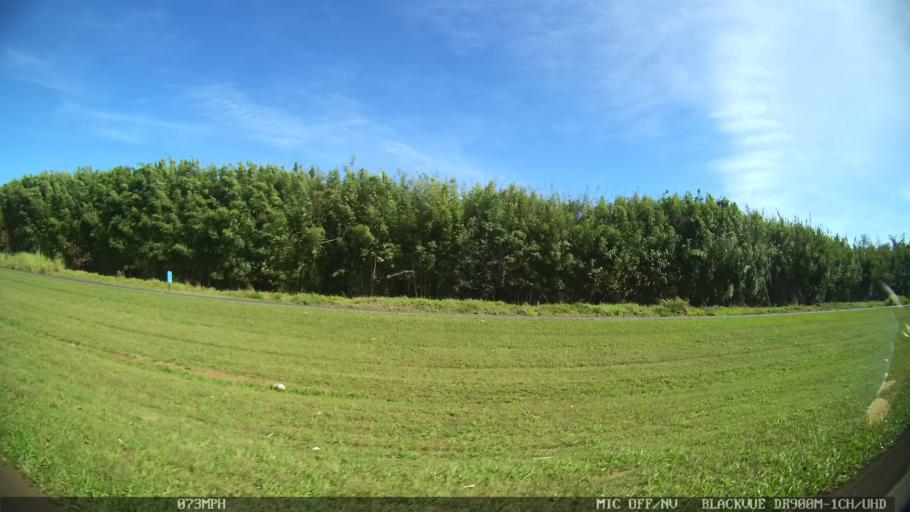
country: BR
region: Sao Paulo
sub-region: Araras
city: Araras
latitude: -22.2826
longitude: -47.3931
